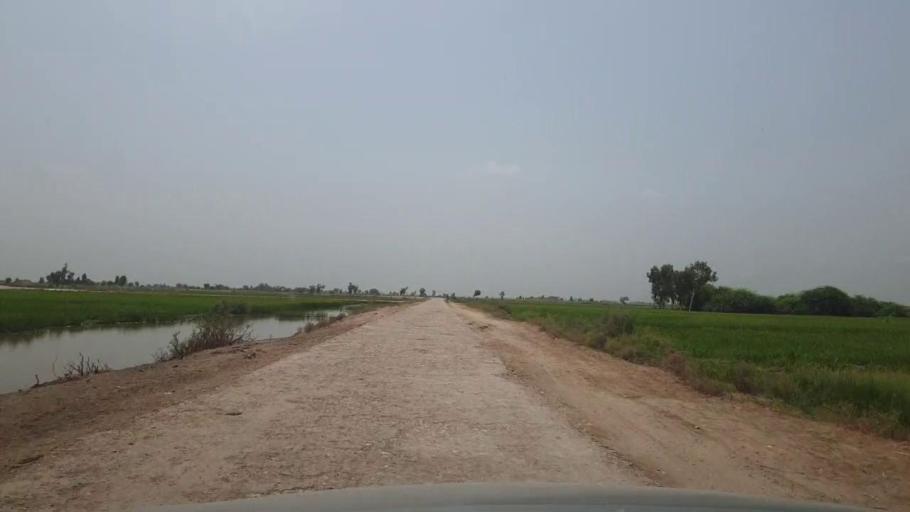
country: PK
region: Sindh
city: Garhi Yasin
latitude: 27.9396
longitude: 68.3894
